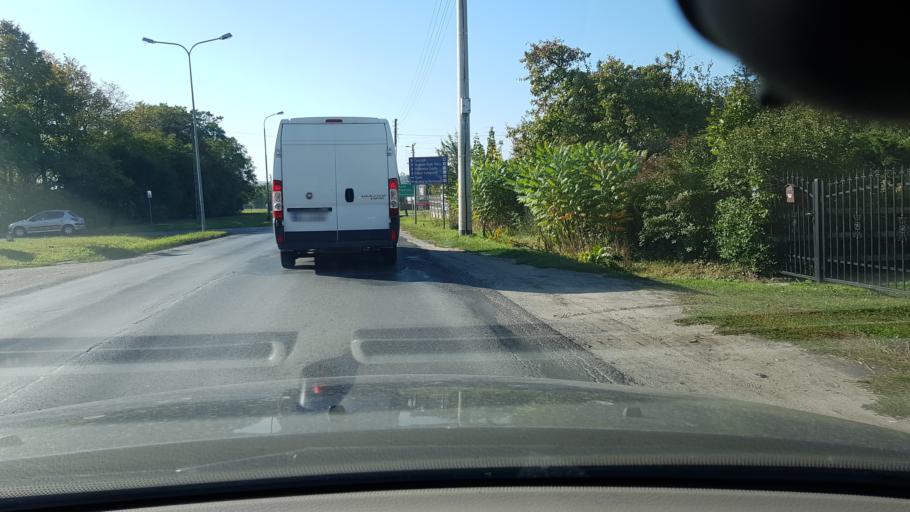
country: PL
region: Lodz Voivodeship
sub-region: Powiat tomaszowski
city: Tomaszow Mazowiecki
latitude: 51.5578
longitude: 20.0195
